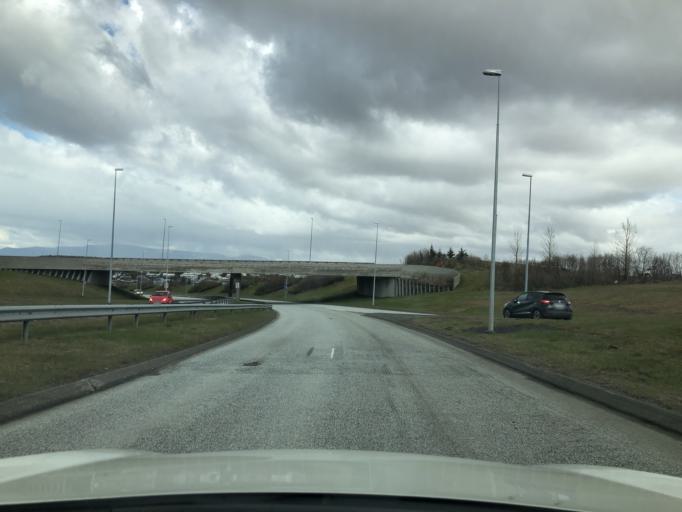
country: IS
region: Capital Region
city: Hafnarfjoerdur
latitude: 64.0595
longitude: -21.9415
